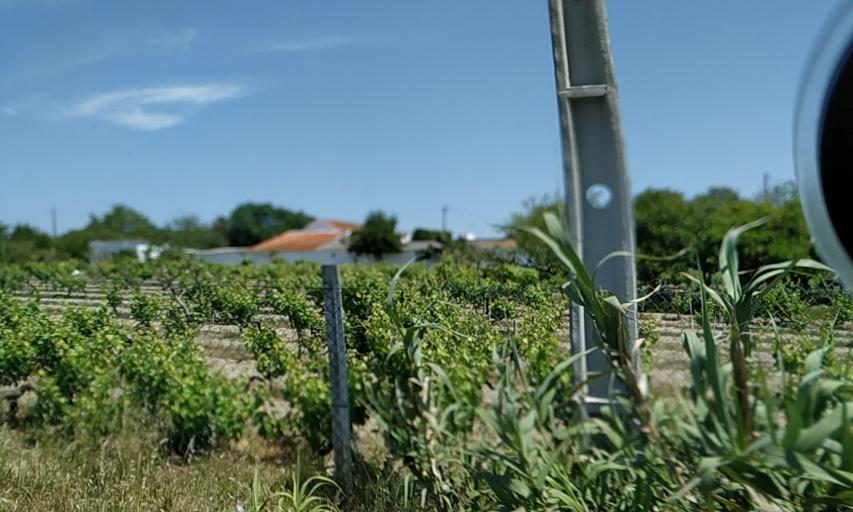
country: PT
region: Santarem
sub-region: Benavente
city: Poceirao
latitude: 38.6909
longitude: -8.7300
